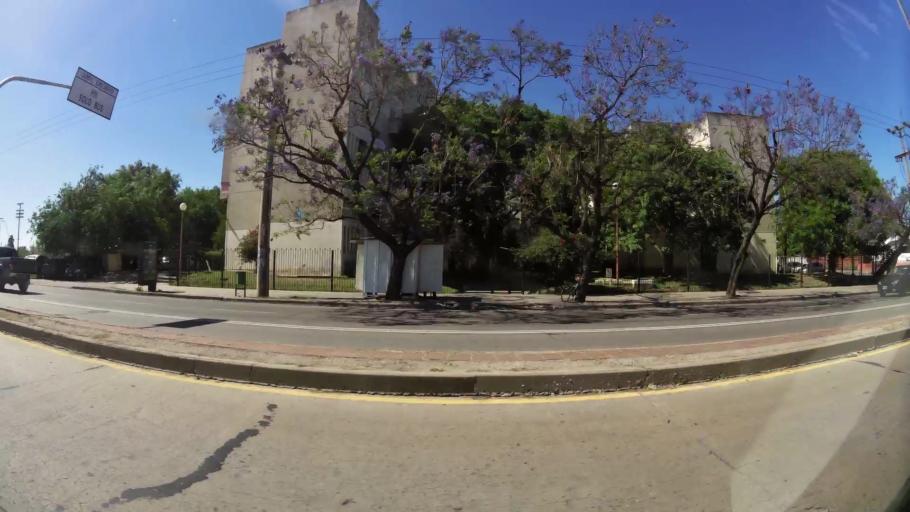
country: AR
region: Cordoba
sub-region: Departamento de Capital
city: Cordoba
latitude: -31.4332
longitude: -64.1455
